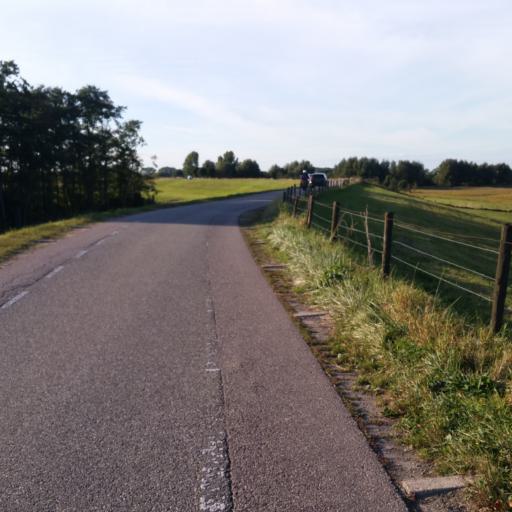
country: NL
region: Utrecht
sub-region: Gemeente IJsselstein
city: IJsselstein
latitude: 51.9770
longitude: 5.0209
